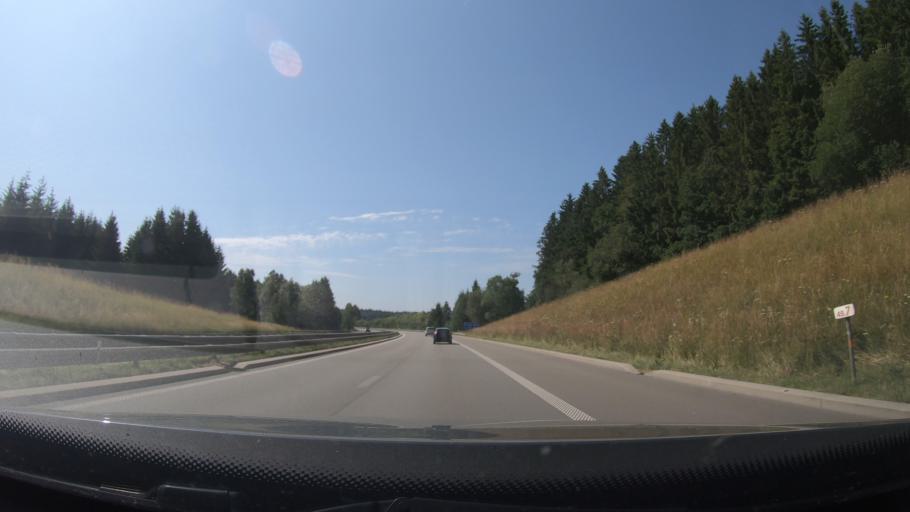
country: BE
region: Wallonia
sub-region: Province de Liege
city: Saint-Vith
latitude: 50.3045
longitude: 6.0792
